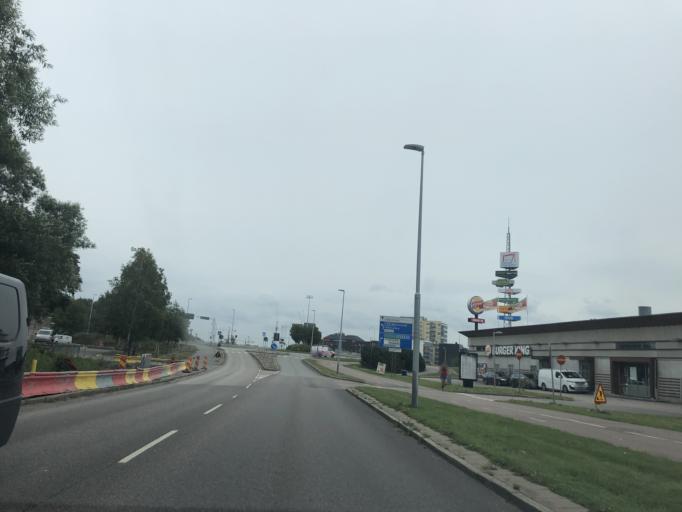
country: SE
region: Vaestra Goetaland
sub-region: Goteborg
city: Majorna
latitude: 57.7098
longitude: 11.9206
